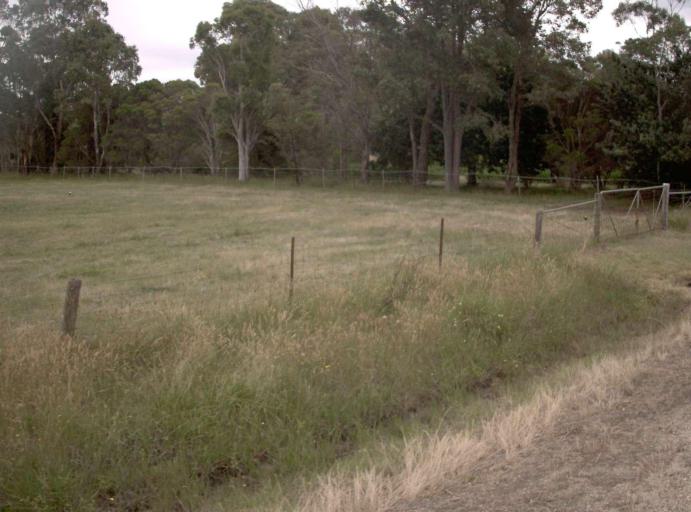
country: AU
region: Victoria
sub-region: East Gippsland
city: Bairnsdale
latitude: -37.8576
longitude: 147.5641
